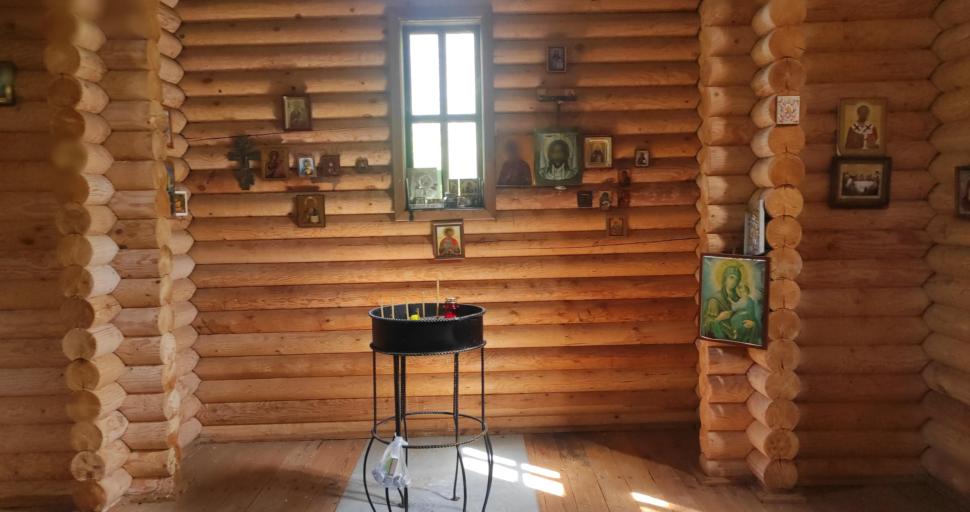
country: RU
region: Leningrad
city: Vysotsk
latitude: 60.6272
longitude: 28.4904
